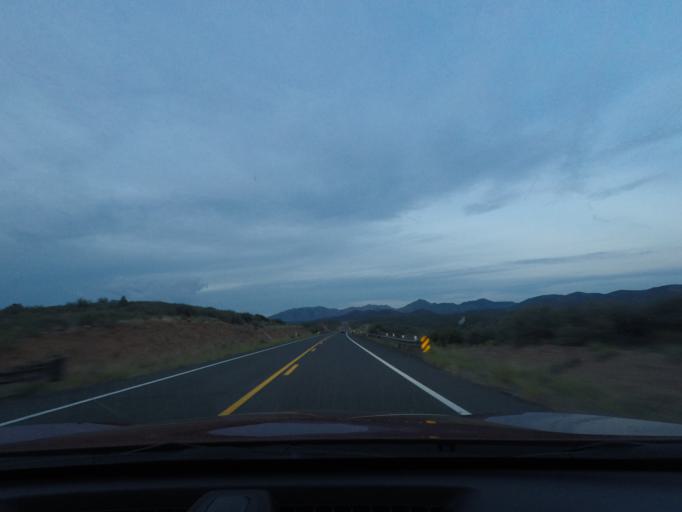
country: US
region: Arizona
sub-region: Yavapai County
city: Williamson
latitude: 34.5685
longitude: -112.6564
